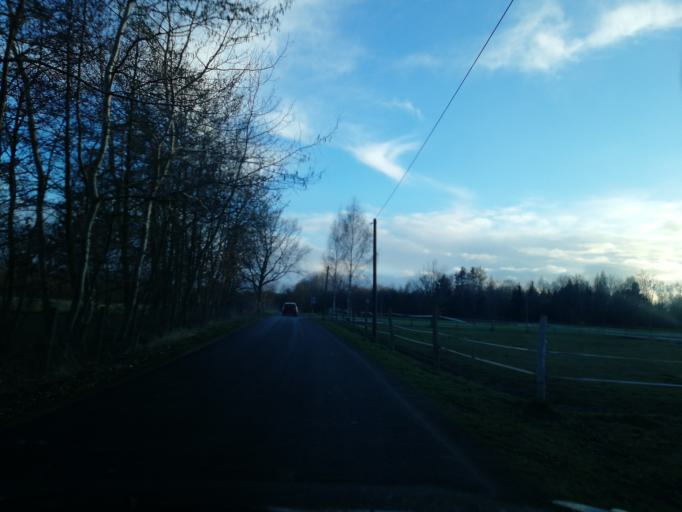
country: DE
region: Brandenburg
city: Calau
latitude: 51.7355
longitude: 13.9608
